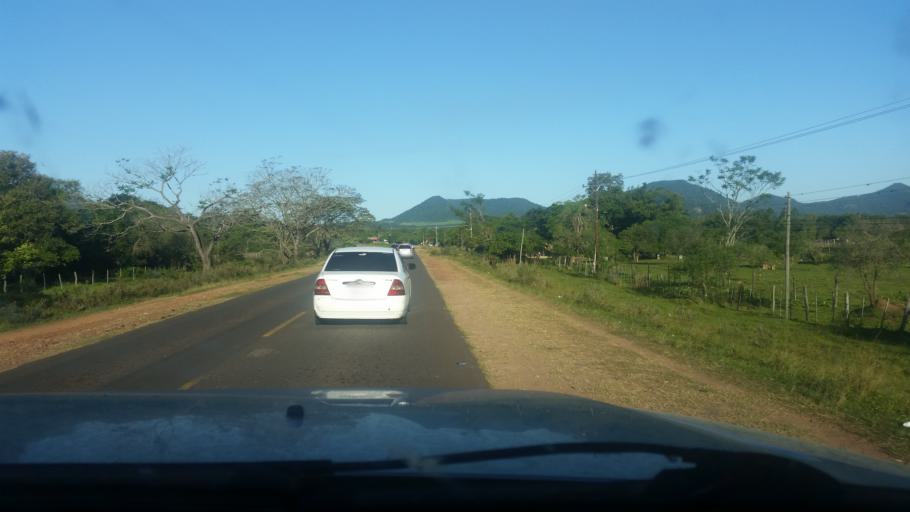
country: PY
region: Guaira
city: Mbocayaty
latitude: -25.7207
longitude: -56.3291
